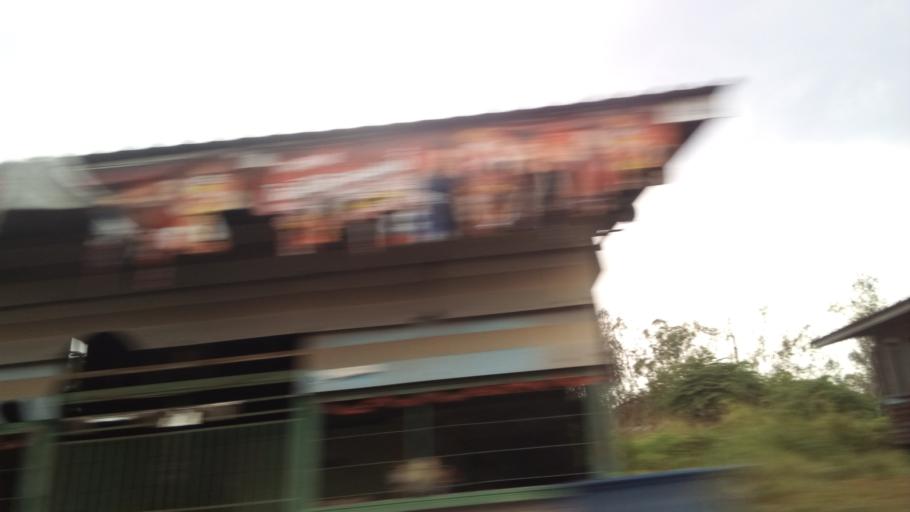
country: TH
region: Phra Nakhon Si Ayutthaya
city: Phra Nakhon Si Ayutthaya
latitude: 14.3397
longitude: 100.5423
